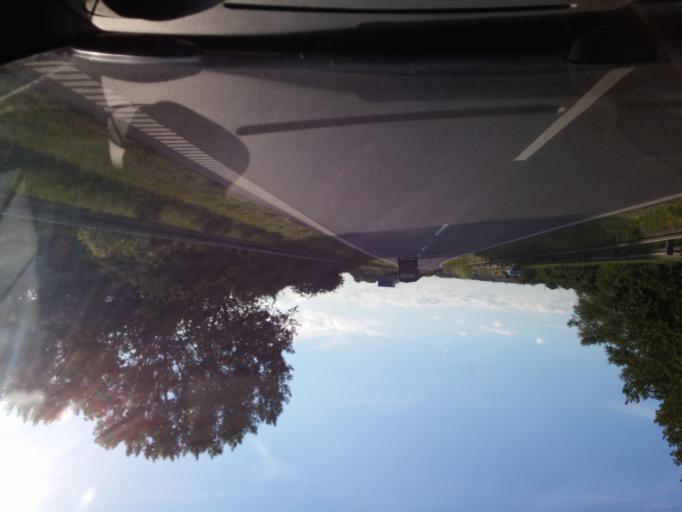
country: DK
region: Zealand
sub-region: Slagelse Kommune
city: Korsor
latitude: 55.3597
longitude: 11.1624
